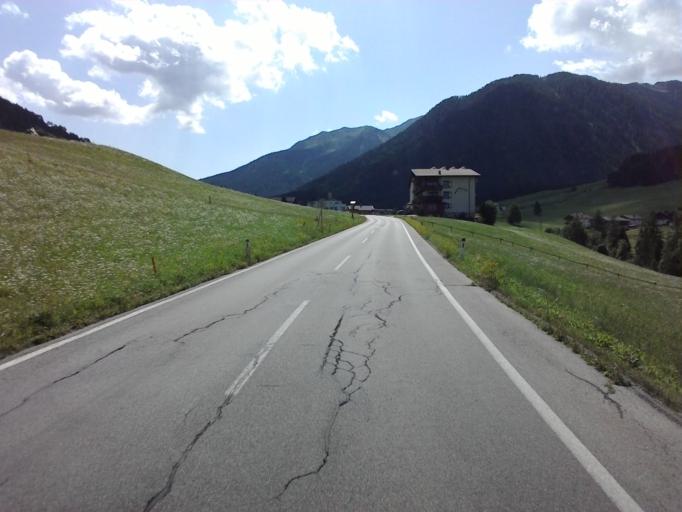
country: AT
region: Tyrol
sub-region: Politischer Bezirk Lienz
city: Kartitsch
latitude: 46.7295
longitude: 12.4907
